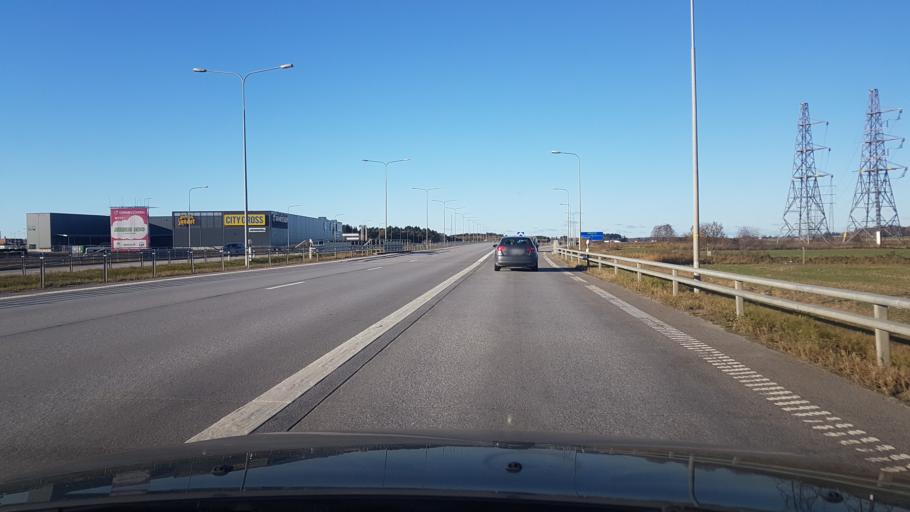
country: SE
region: Uppsala
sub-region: Uppsala Kommun
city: Gamla Uppsala
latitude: 59.8851
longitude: 17.6782
